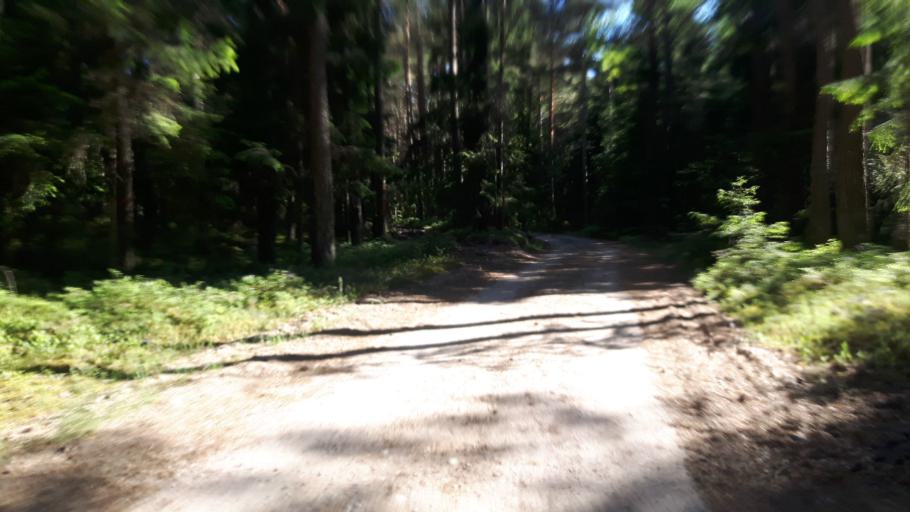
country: LV
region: Salacgrivas
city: Salacgriva
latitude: 57.7271
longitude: 24.3496
